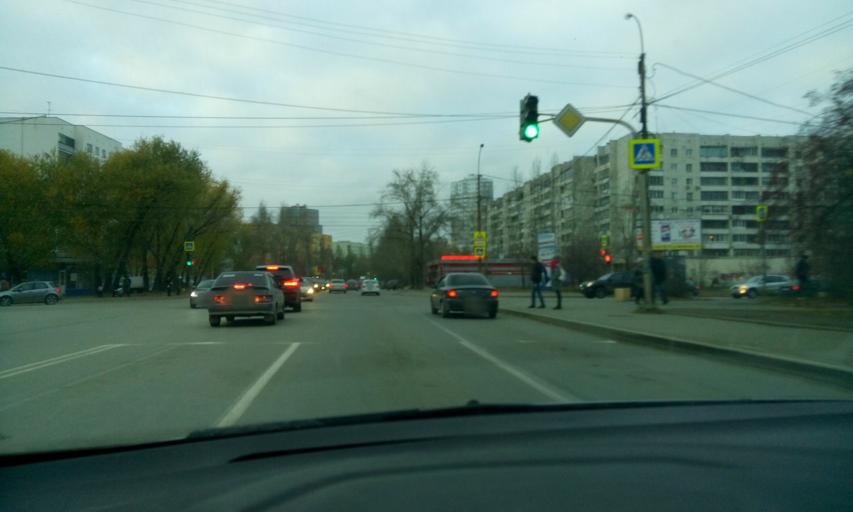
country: RU
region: Sverdlovsk
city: Yekaterinburg
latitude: 56.9021
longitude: 60.6253
